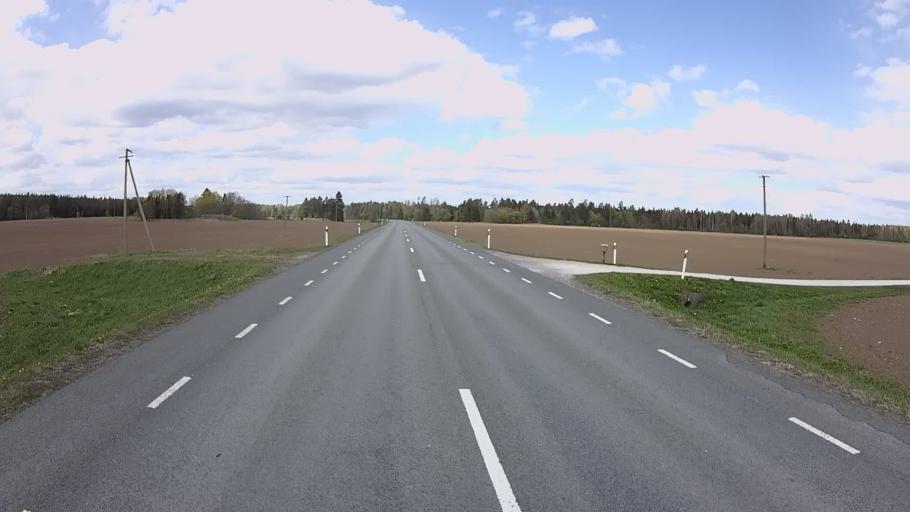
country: EE
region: Jaervamaa
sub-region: Jaerva-Jaani vald
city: Jarva-Jaani
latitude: 59.0870
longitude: 25.8360
